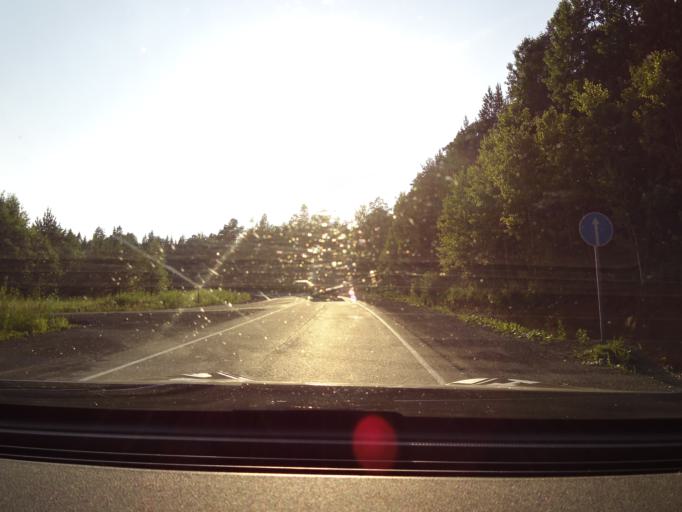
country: RU
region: Sverdlovsk
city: Druzhinino
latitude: 56.8006
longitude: 59.4663
